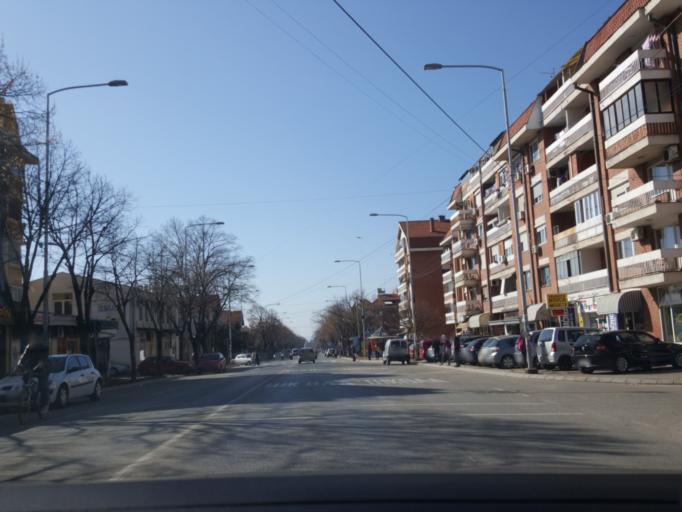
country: RS
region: Central Serbia
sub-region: Nisavski Okrug
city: Nis
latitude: 43.3296
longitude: 21.9285
